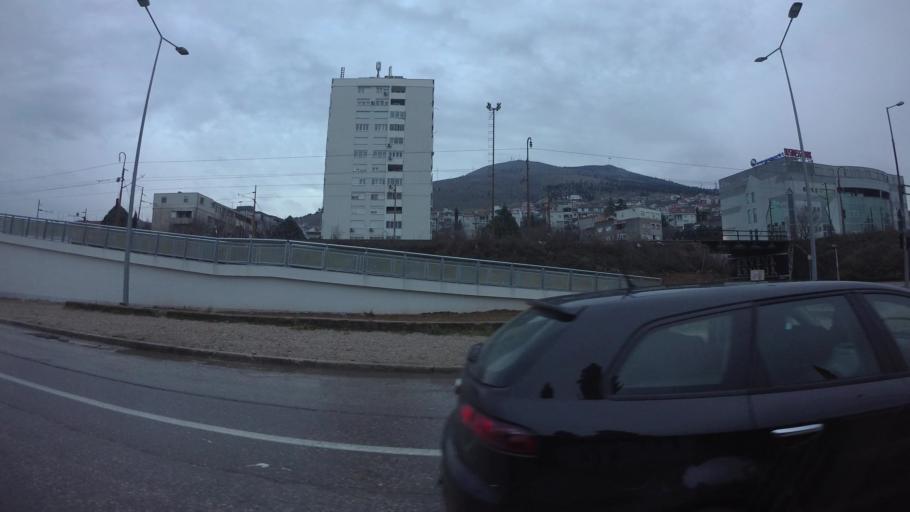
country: BA
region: Federation of Bosnia and Herzegovina
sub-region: Hercegovacko-Bosanski Kanton
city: Mostar
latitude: 43.3560
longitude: 17.8127
